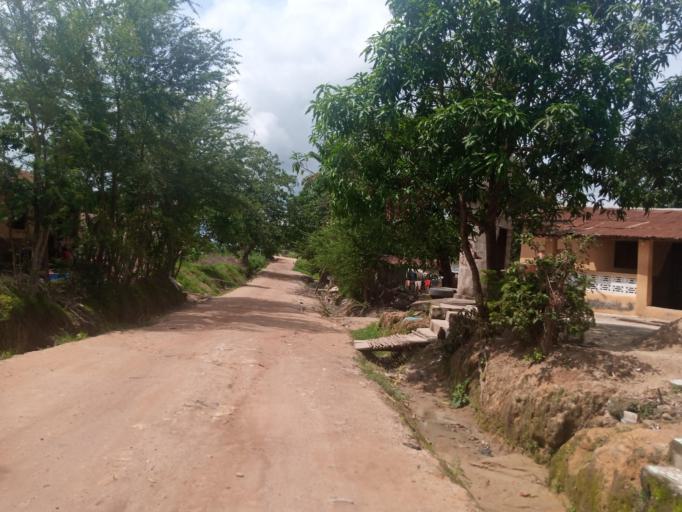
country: SL
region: Southern Province
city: Bo
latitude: 7.9639
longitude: -11.7542
